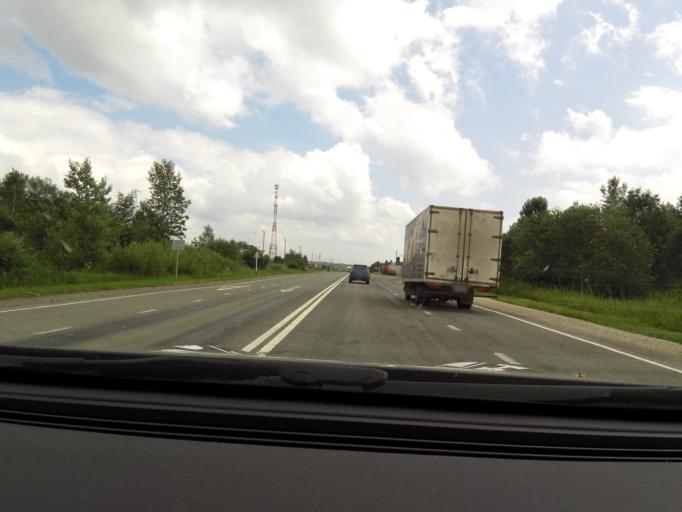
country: RU
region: Sverdlovsk
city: Achit
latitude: 56.8595
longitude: 57.6962
